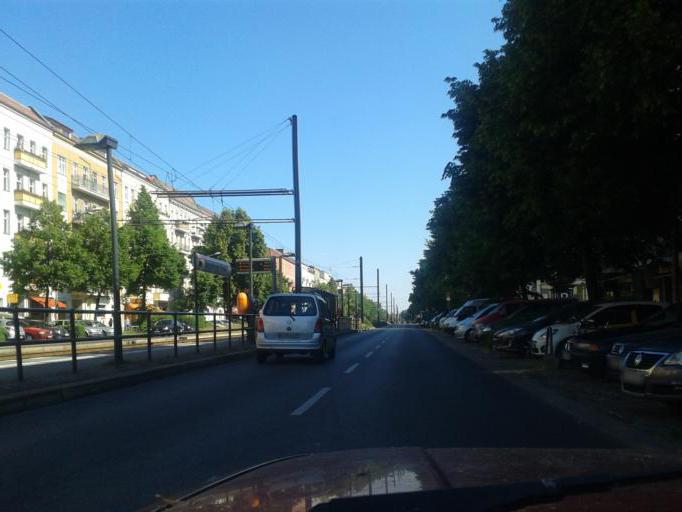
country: DE
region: Berlin
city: Prenzlauer Berg Bezirk
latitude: 52.5357
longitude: 13.4224
